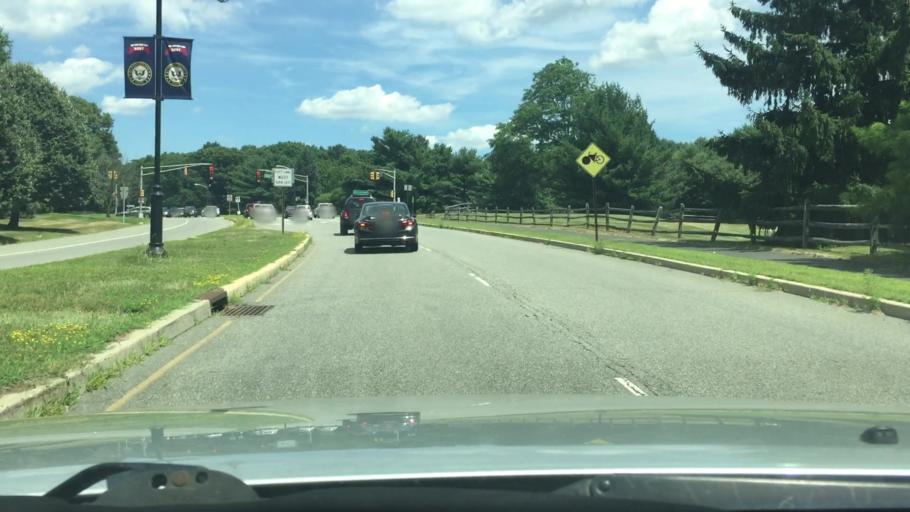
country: US
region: New Jersey
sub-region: Middlesex County
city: East Brunswick
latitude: 40.4201
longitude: -74.4013
